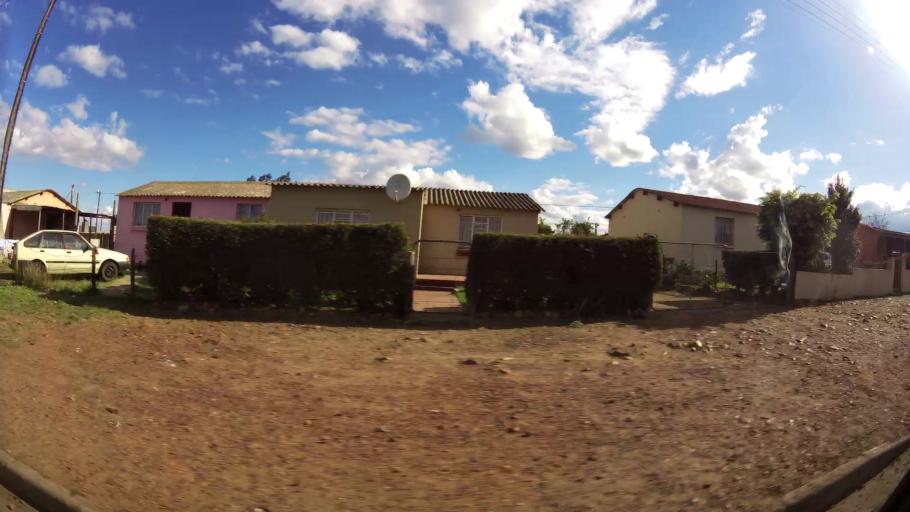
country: ZA
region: Western Cape
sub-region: Overberg District Municipality
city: Swellendam
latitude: -34.0402
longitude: 20.4407
